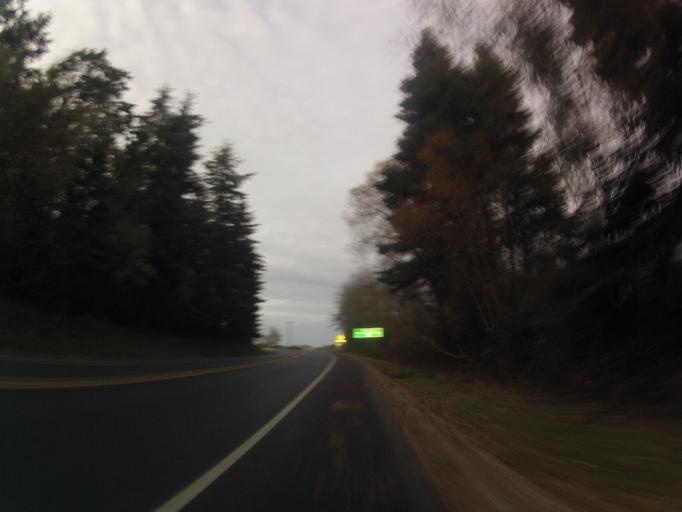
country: US
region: Washington
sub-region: Island County
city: Coupeville
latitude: 48.1681
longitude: -122.6779
